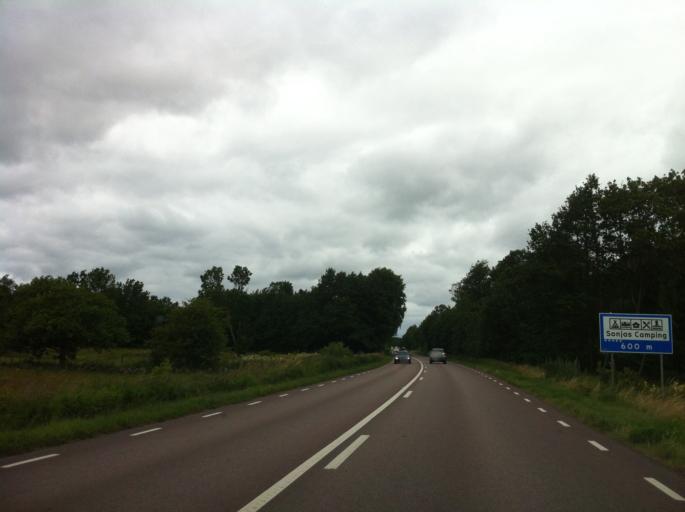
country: SE
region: Kalmar
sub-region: Borgholms Kommun
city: Borgholm
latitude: 57.1764
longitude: 17.0282
